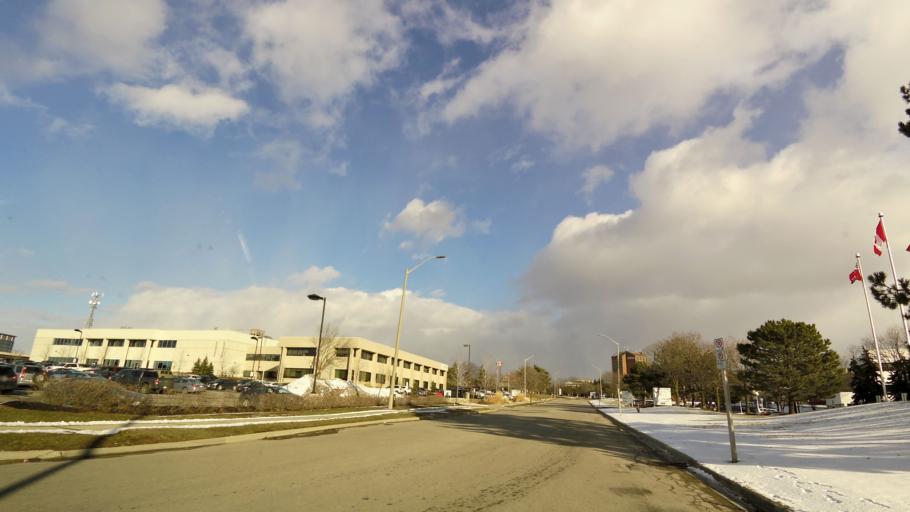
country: CA
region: Ontario
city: Brampton
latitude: 43.6021
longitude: -79.7488
